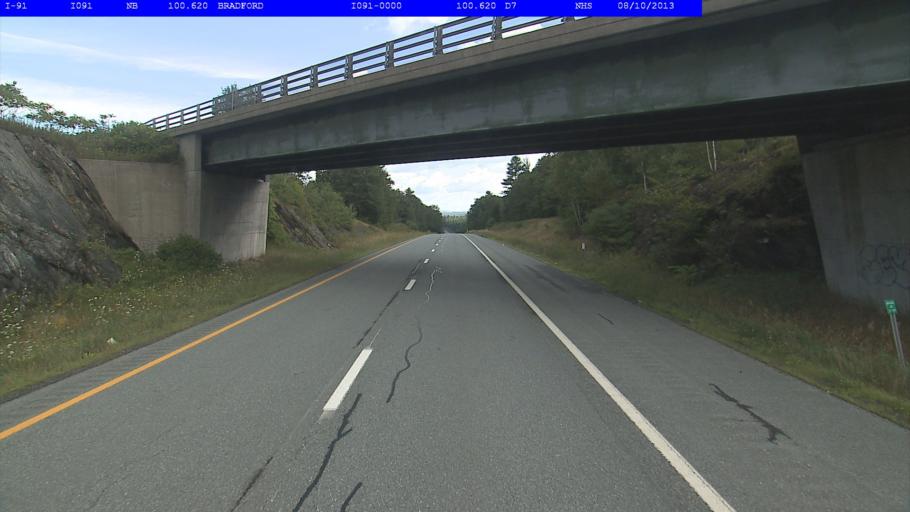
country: US
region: New Hampshire
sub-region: Grafton County
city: Haverhill
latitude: 44.0234
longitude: -72.1166
